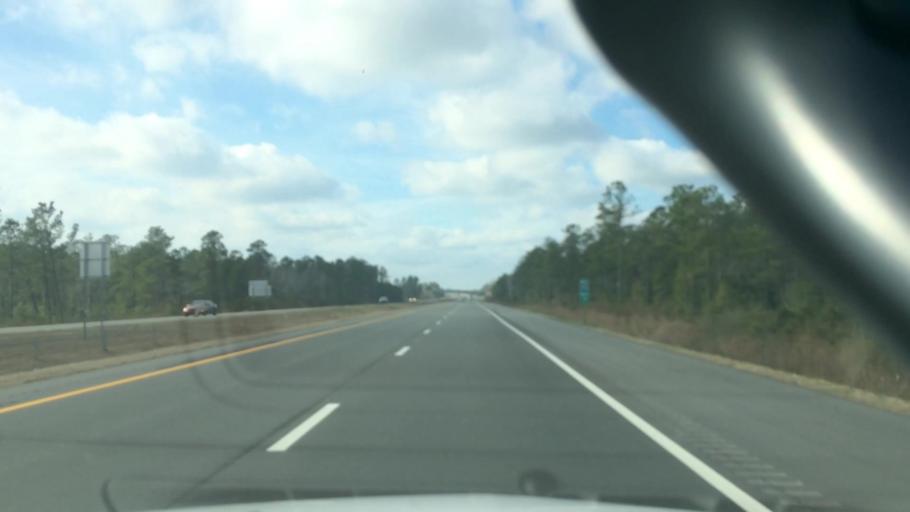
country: US
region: North Carolina
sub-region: Brunswick County
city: Leland
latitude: 34.2755
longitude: -78.0396
